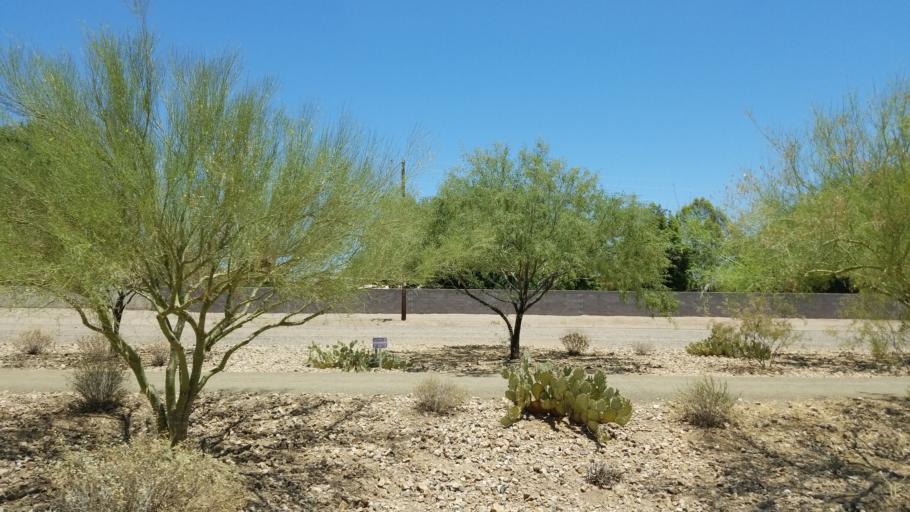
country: US
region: Arizona
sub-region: Maricopa County
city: Tolleson
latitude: 33.5105
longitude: -112.2903
